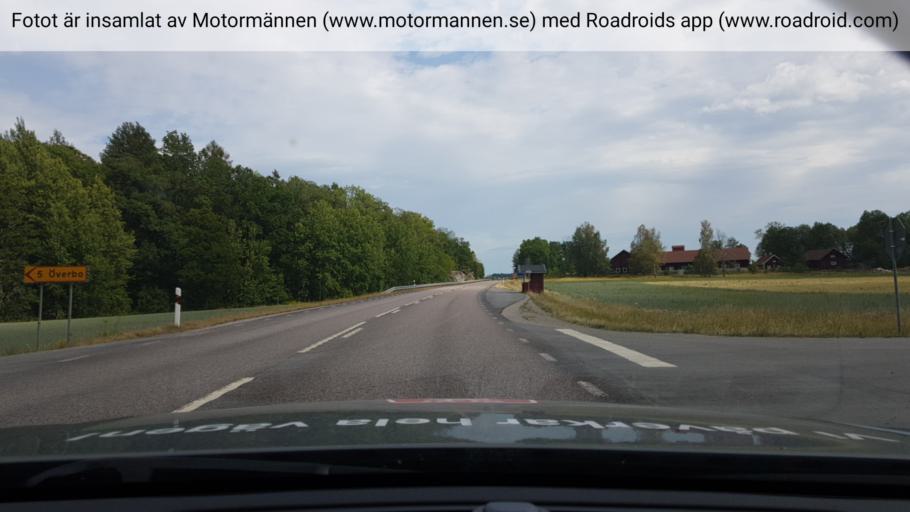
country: SE
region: Uppsala
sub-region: Enkopings Kommun
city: Orsundsbro
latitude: 59.8776
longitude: 17.2856
